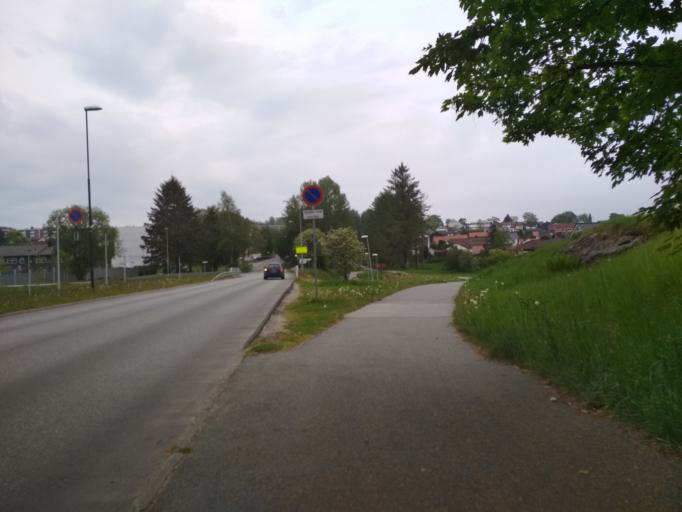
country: NO
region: Rogaland
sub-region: Stavanger
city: Stavanger
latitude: 58.9531
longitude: 5.6873
